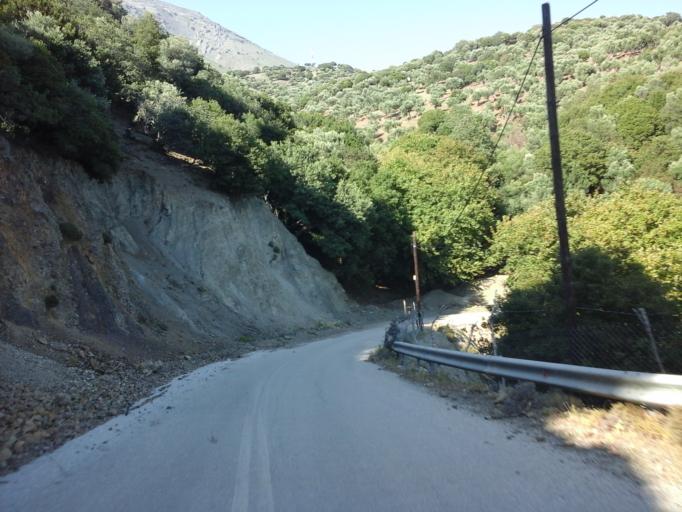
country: GR
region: East Macedonia and Thrace
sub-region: Nomos Evrou
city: Samothraki
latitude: 40.4191
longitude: 25.5441
